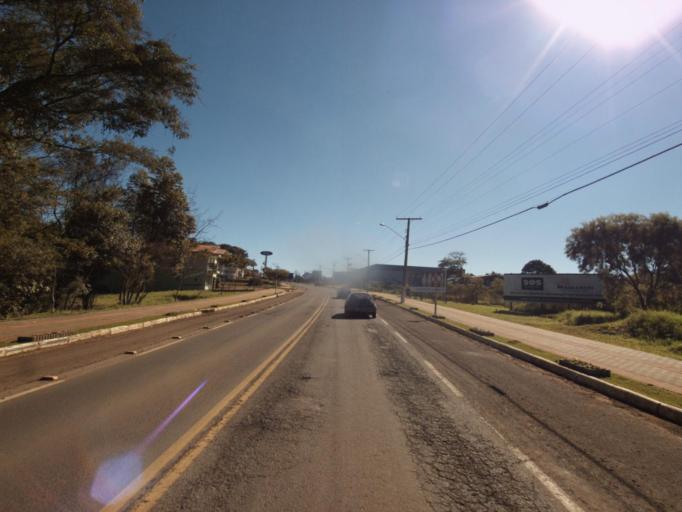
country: AR
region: Misiones
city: Bernardo de Irigoyen
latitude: -26.7535
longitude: -53.5092
